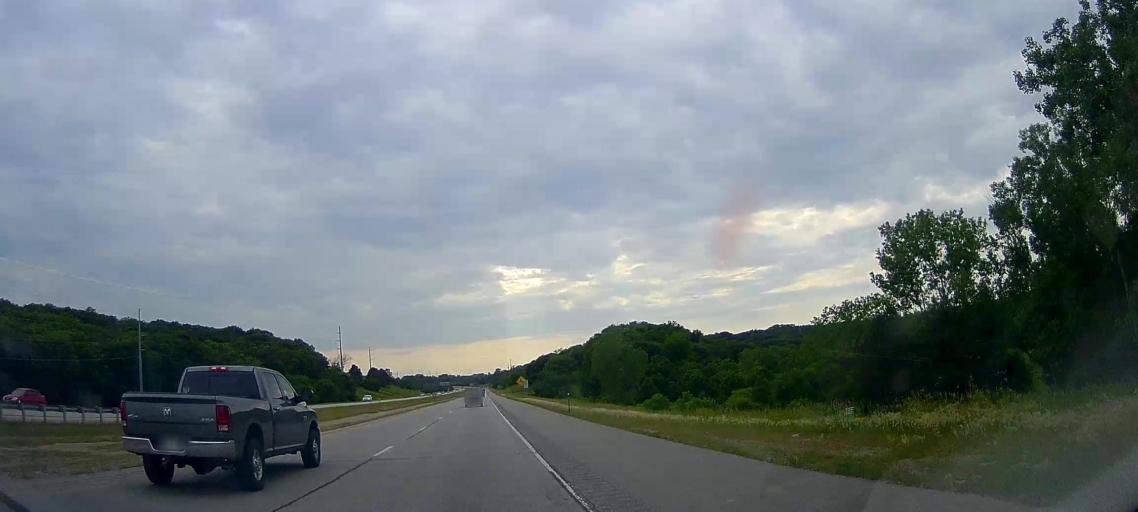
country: US
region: Iowa
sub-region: Pottawattamie County
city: Carter Lake
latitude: 41.3469
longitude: -95.9952
